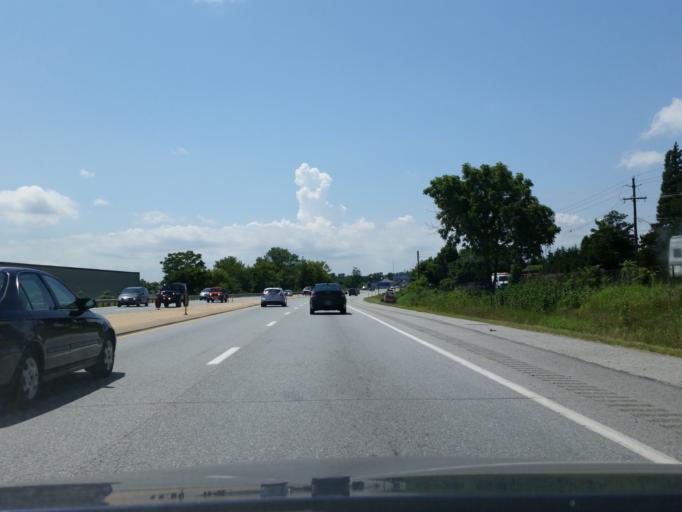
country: US
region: Pennsylvania
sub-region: York County
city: North York
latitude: 39.9825
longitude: -76.7102
